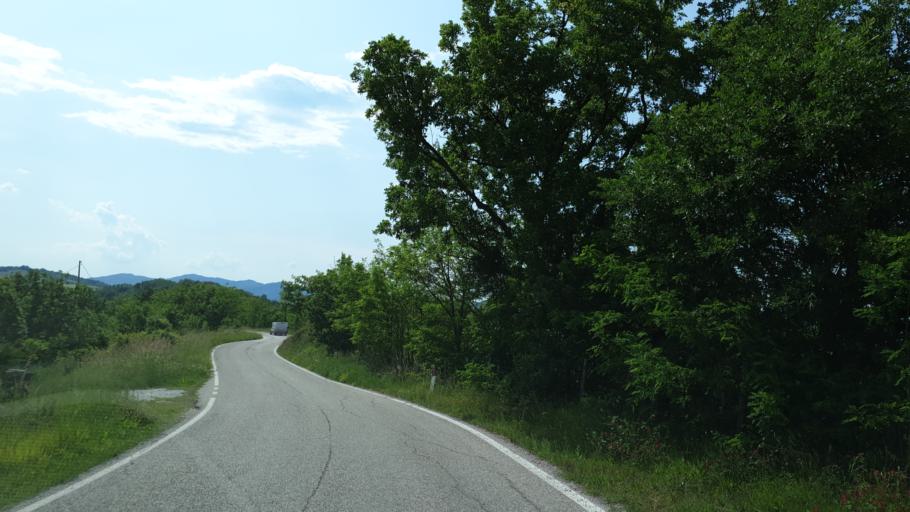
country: IT
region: Emilia-Romagna
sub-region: Provincia di Rimini
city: Sant'Agata Feltria
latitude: 43.9116
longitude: 12.2086
